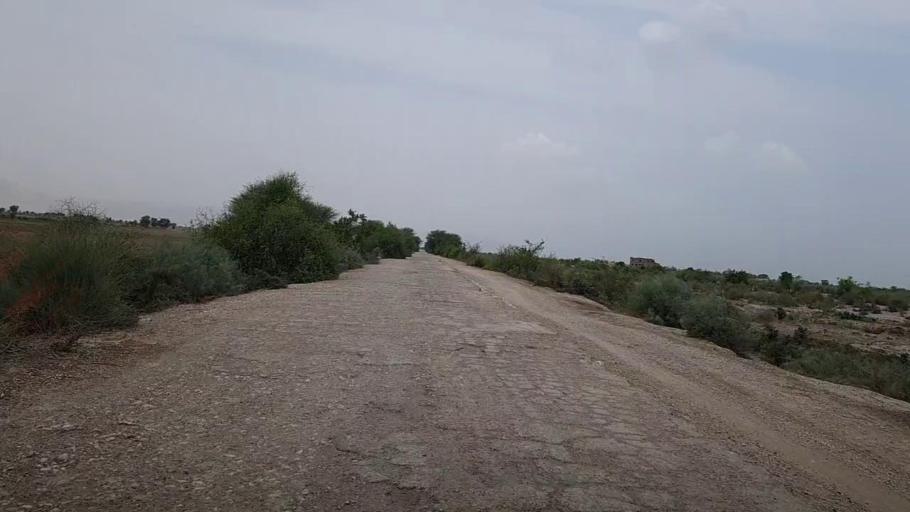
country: PK
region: Sindh
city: Sann
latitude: 26.2026
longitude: 67.9711
